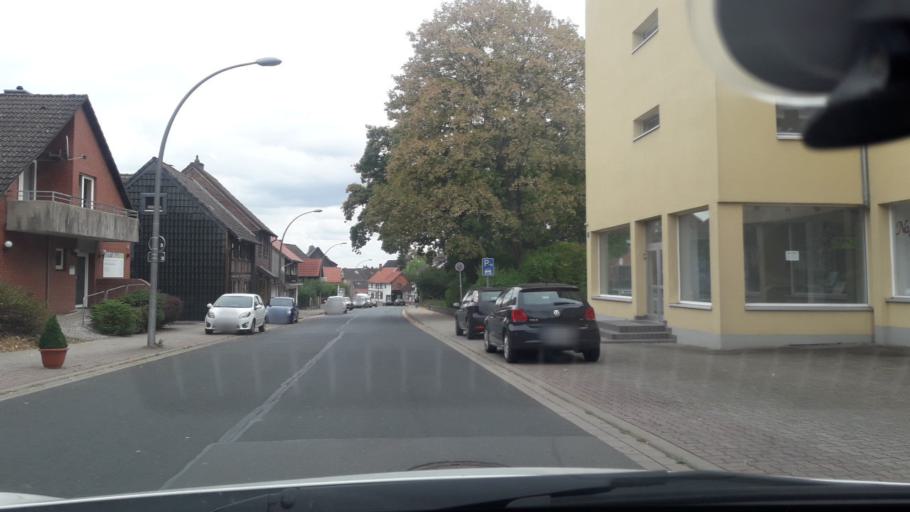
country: DE
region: Lower Saxony
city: Elbe
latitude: 52.1067
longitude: 10.3533
